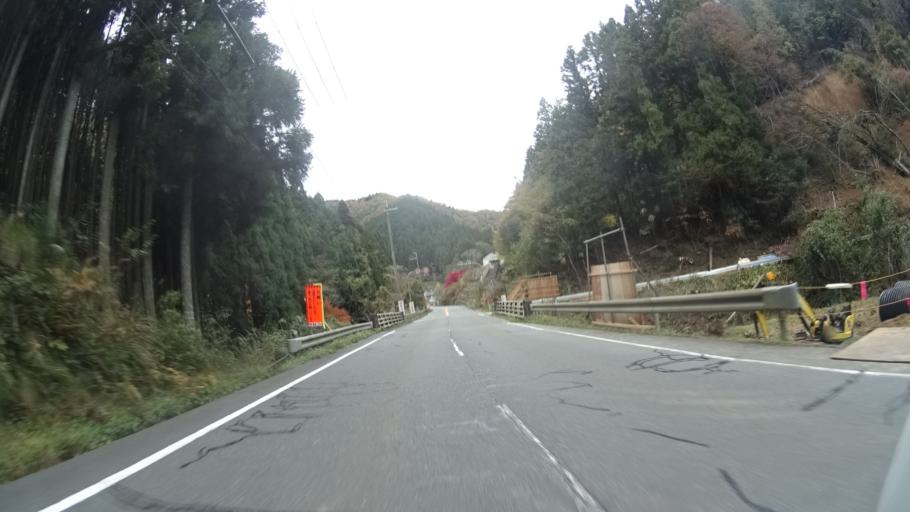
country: JP
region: Kyoto
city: Ayabe
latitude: 35.2431
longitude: 135.2953
